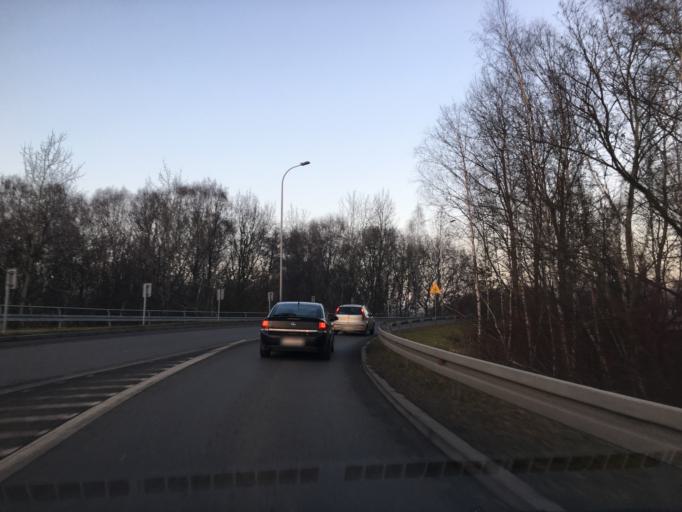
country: PL
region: Silesian Voivodeship
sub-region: Powiat tarnogorski
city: Radzionkow
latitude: 50.3695
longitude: 18.8762
